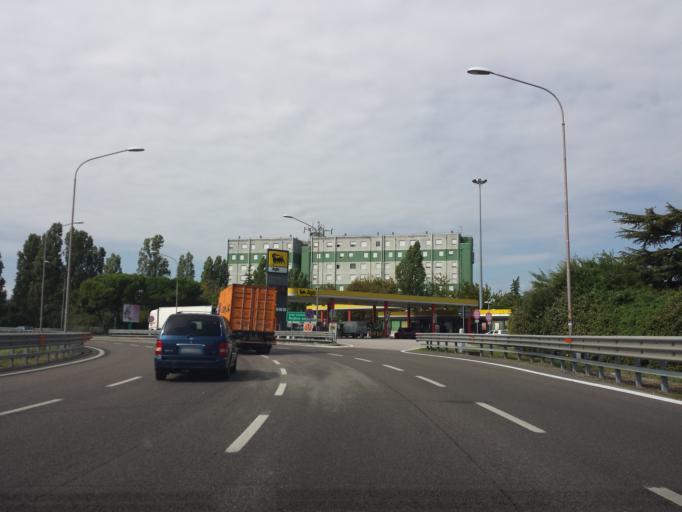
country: IT
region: Veneto
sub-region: Provincia di Venezia
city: Mestre
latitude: 45.4751
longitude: 12.2124
